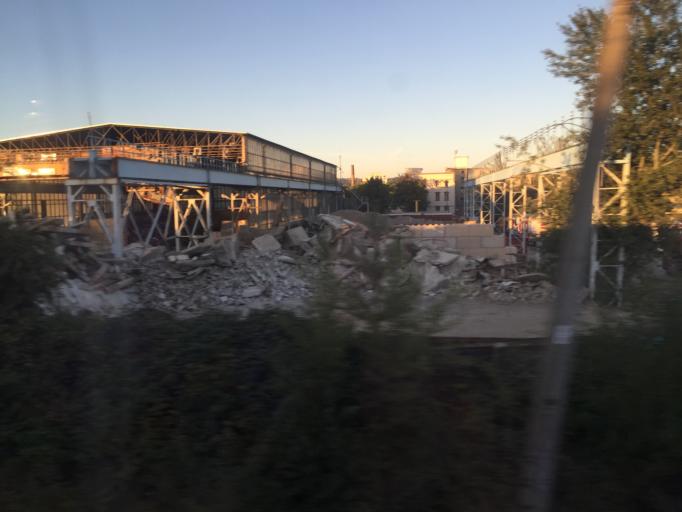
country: DE
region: Saxony
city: Heidenau
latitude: 51.0068
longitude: 13.8165
